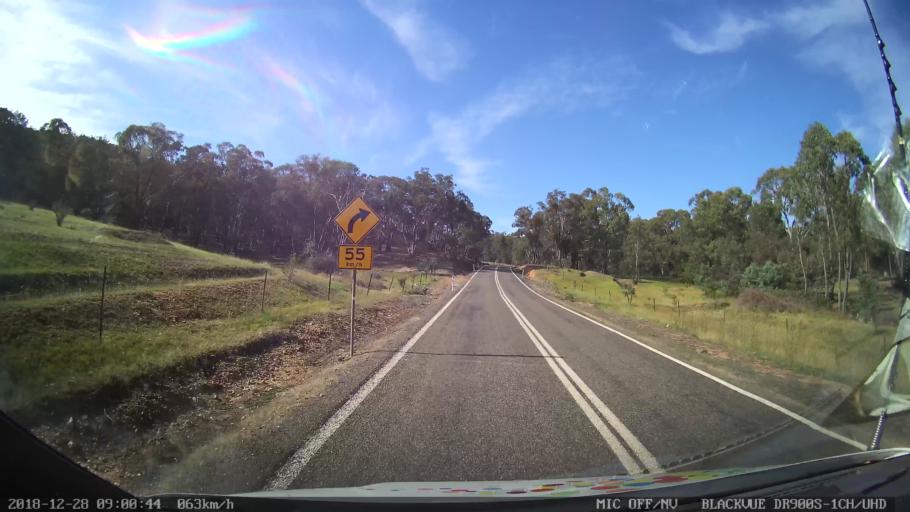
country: AU
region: New South Wales
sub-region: Upper Lachlan Shire
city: Crookwell
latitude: -34.1410
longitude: 149.3348
